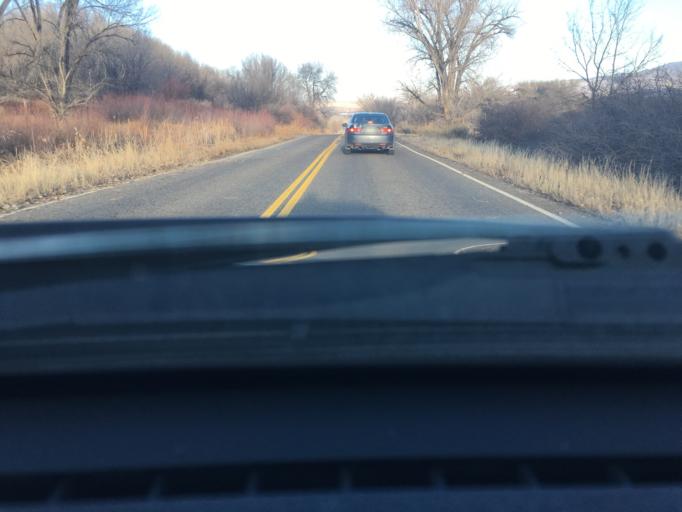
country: US
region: Colorado
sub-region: Delta County
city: Delta
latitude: 38.7436
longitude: -108.1134
